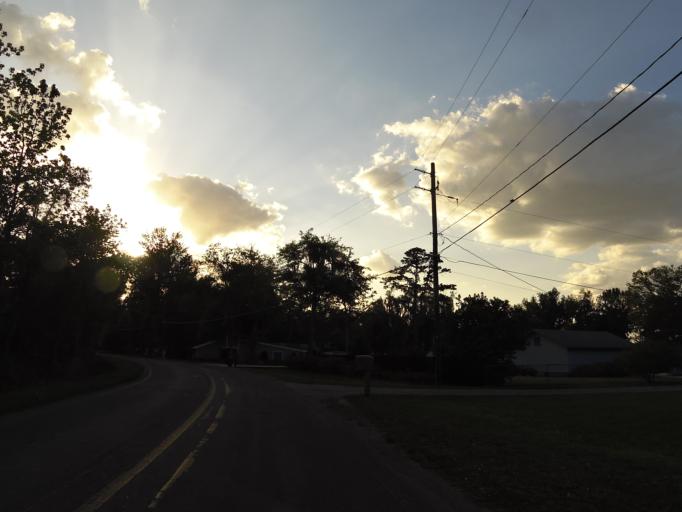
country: US
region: Florida
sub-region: Saint Johns County
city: Fruit Cove
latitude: 30.1287
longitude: -81.6120
